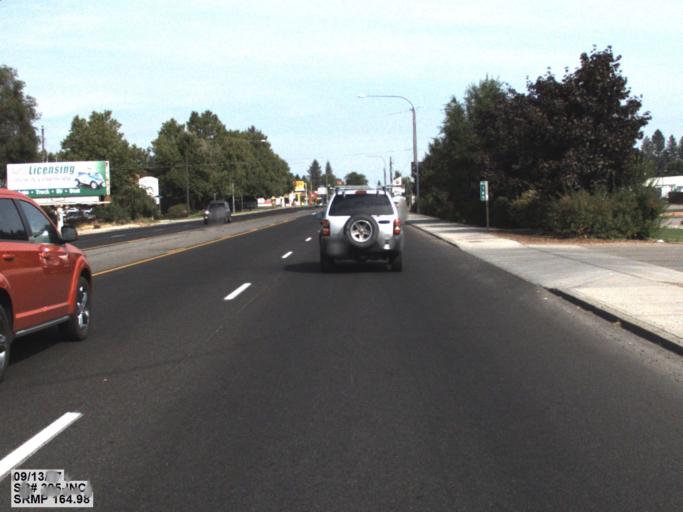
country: US
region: Washington
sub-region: Spokane County
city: Country Homes
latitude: 47.7461
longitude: -117.4113
